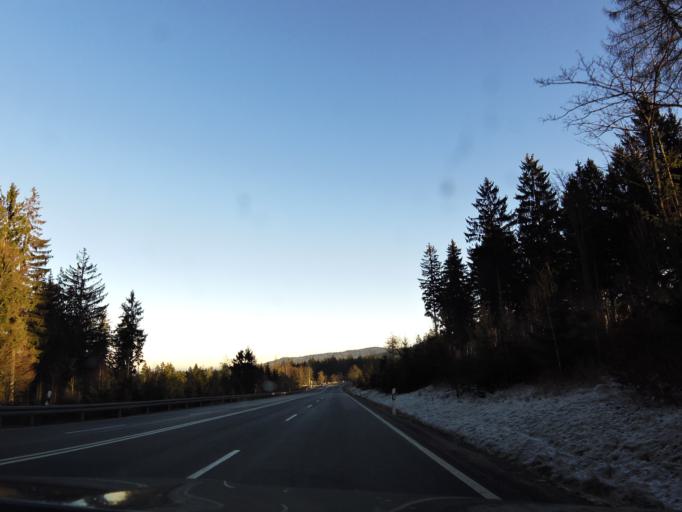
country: DE
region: Bavaria
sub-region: Upper Franconia
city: Nagel
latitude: 50.0055
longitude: 11.9011
